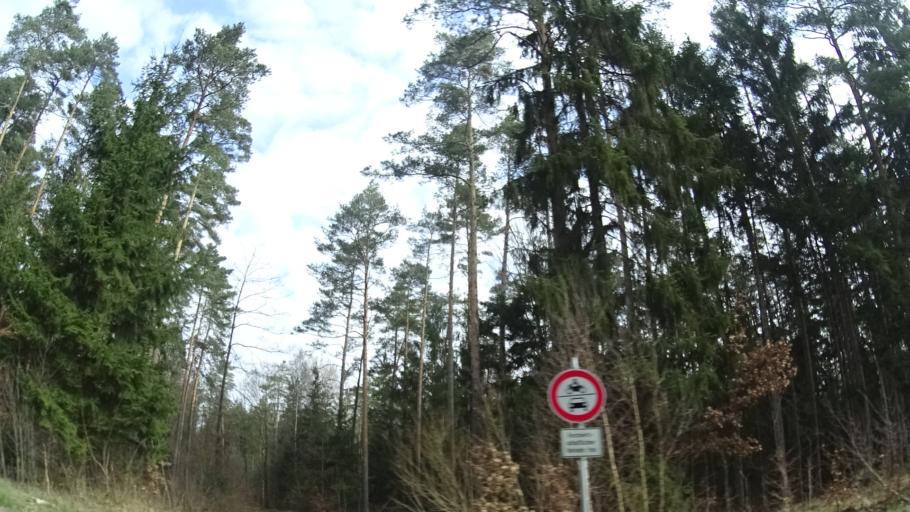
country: DE
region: Bavaria
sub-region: Regierungsbezirk Mittelfranken
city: Winkelhaid
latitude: 49.4106
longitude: 11.2847
